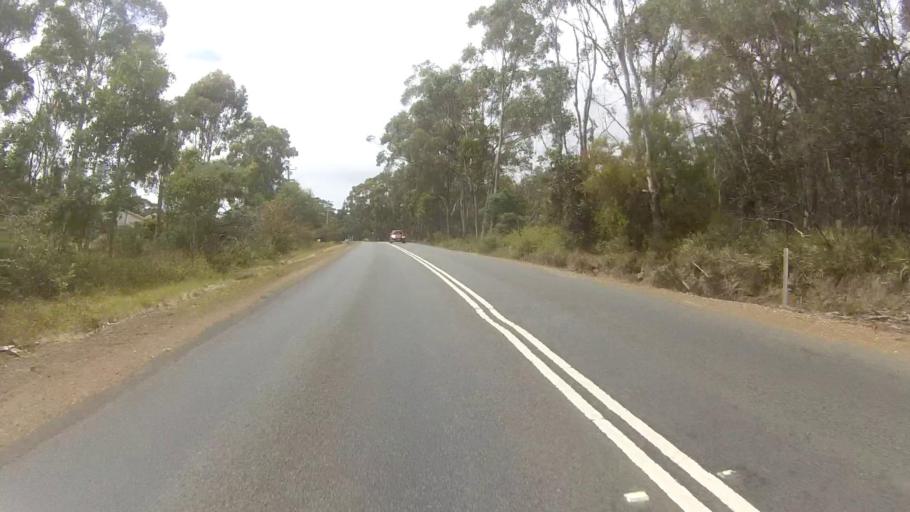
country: AU
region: Tasmania
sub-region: Kingborough
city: Margate
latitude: -42.9966
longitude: 147.2229
